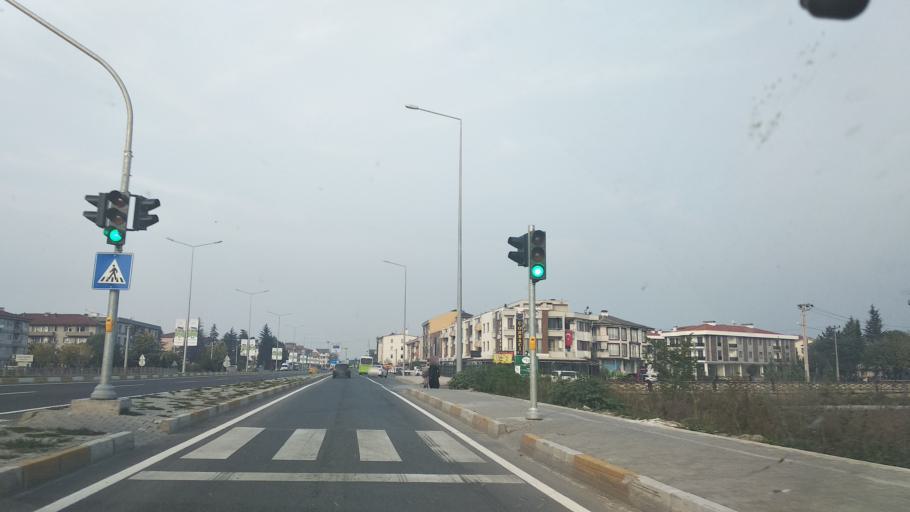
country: TR
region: Duzce
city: Duzce
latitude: 40.8324
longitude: 31.1688
